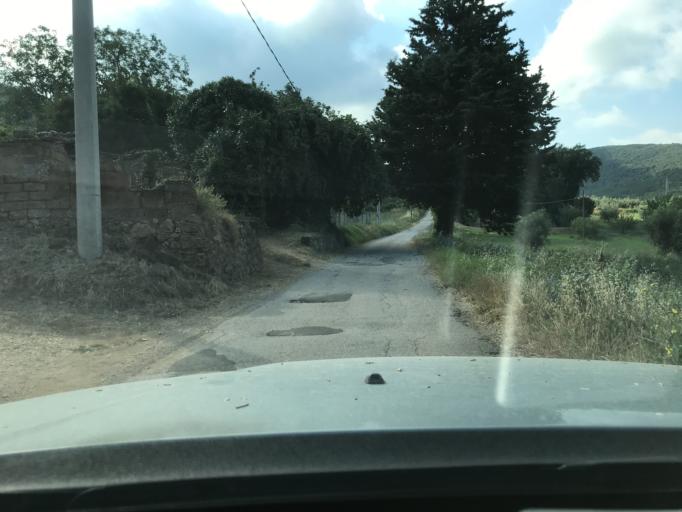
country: IT
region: Umbria
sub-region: Provincia di Terni
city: Guardea
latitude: 42.6293
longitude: 12.3180
